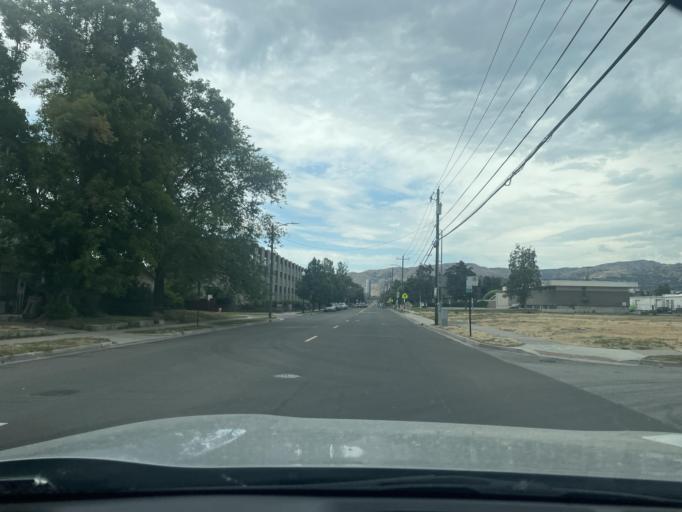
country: US
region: Utah
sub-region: Salt Lake County
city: Salt Lake City
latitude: 40.7432
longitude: -111.8939
